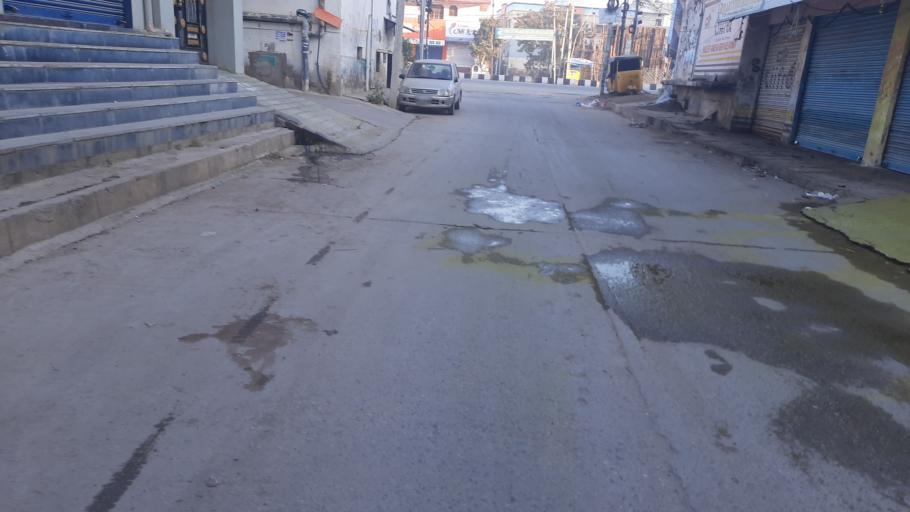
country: IN
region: Telangana
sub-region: Rangareddi
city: Gaddi Annaram
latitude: 17.3447
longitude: 78.5264
